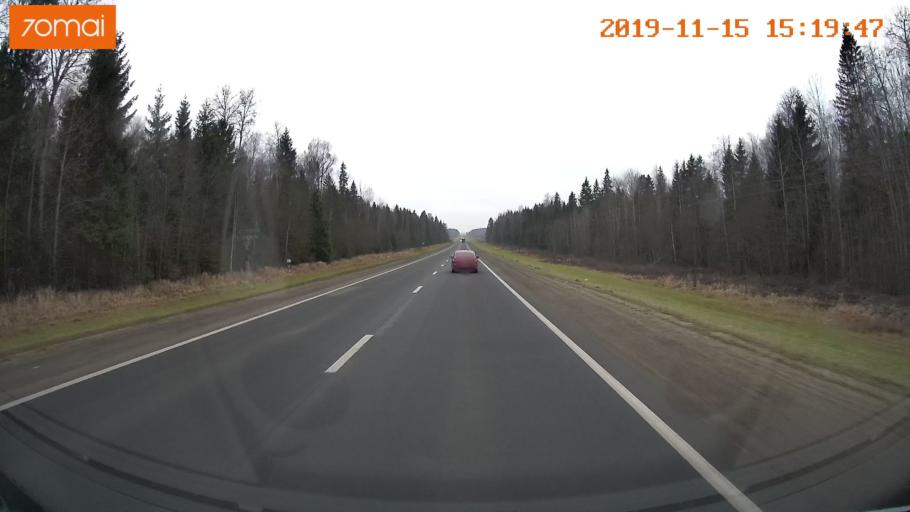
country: RU
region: Jaroslavl
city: Danilov
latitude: 58.2306
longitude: 40.1721
